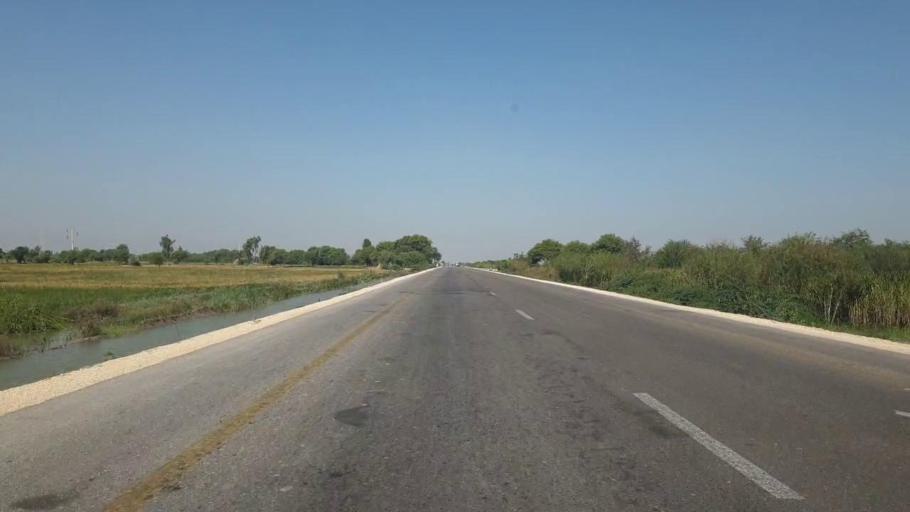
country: PK
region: Sindh
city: Talhar
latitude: 24.8188
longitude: 68.8158
